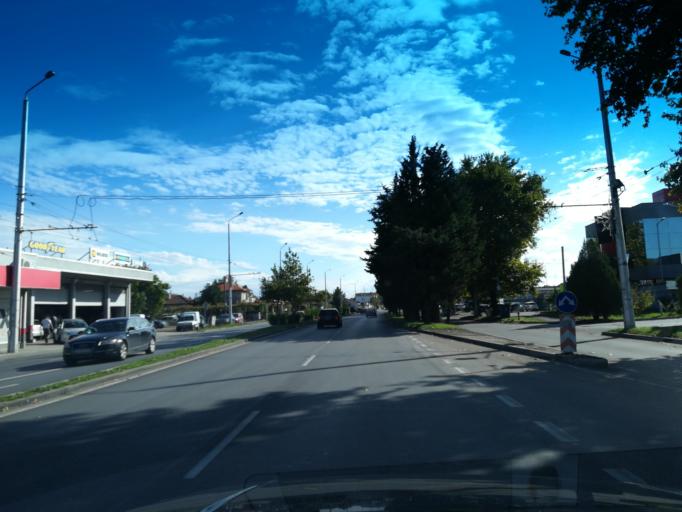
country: BG
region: Stara Zagora
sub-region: Obshtina Stara Zagora
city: Stara Zagora
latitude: 42.4038
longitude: 25.6424
